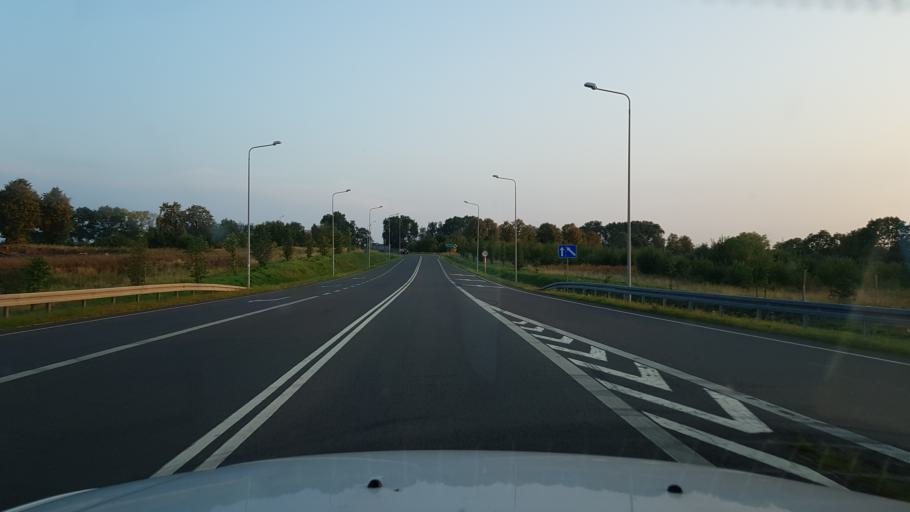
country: PL
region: West Pomeranian Voivodeship
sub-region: Powiat goleniowski
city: Nowogard
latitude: 53.6891
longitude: 15.1365
